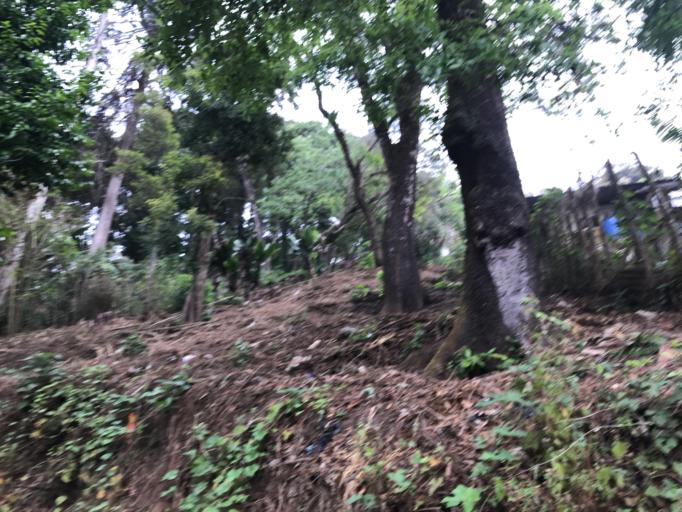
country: GT
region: Guatemala
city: Santa Catarina Pinula
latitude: 14.5423
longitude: -90.4895
